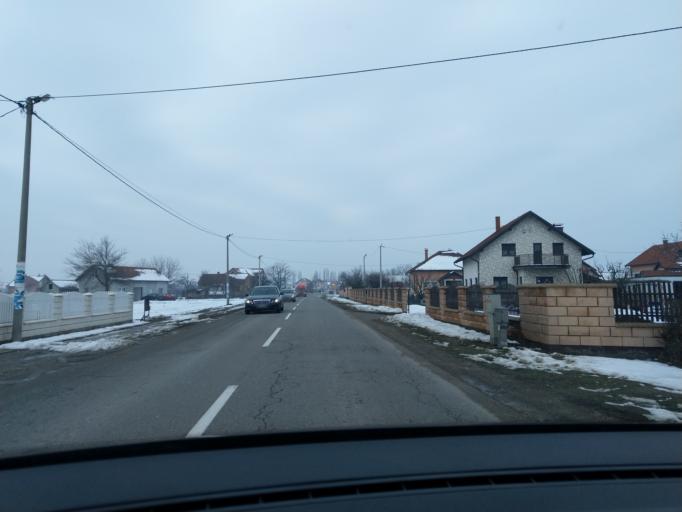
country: BA
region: Republika Srpska
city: Velika Obarska
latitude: 44.7960
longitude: 19.1752
